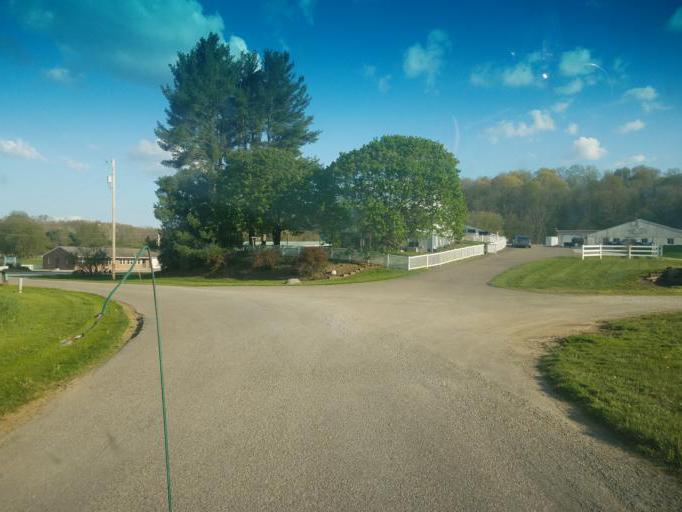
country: US
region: Ohio
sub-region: Wayne County
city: Shreve
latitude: 40.5881
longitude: -82.0112
